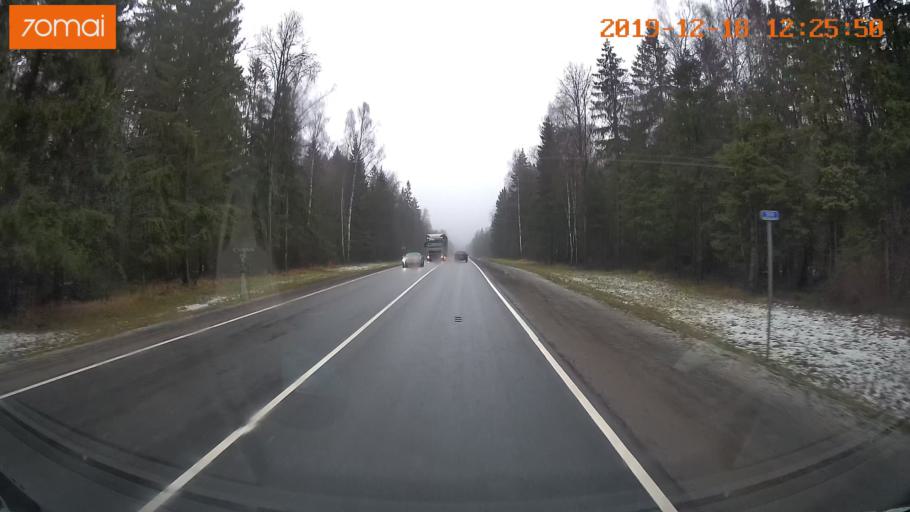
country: RU
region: Moskovskaya
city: Novopetrovskoye
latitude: 56.0436
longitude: 36.4991
